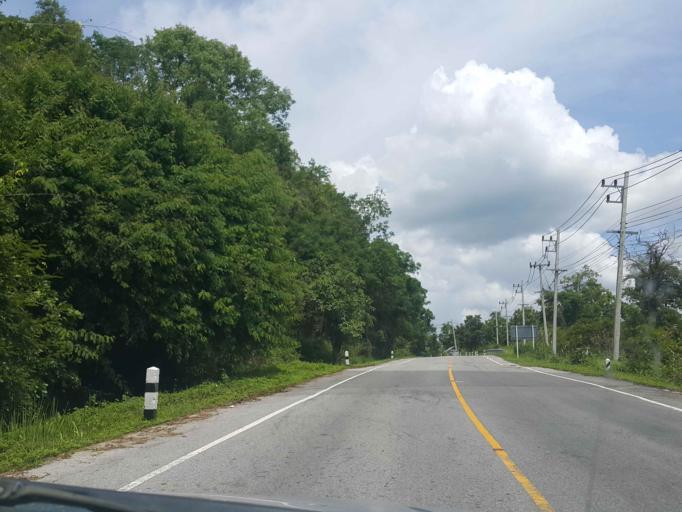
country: TH
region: Nan
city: Ban Luang
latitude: 18.8745
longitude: 100.4883
